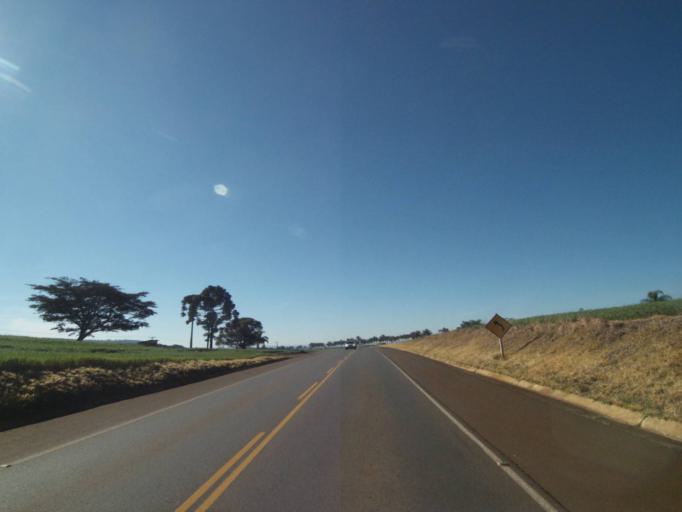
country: BR
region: Parana
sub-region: Tibagi
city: Tibagi
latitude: -24.4233
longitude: -50.3796
